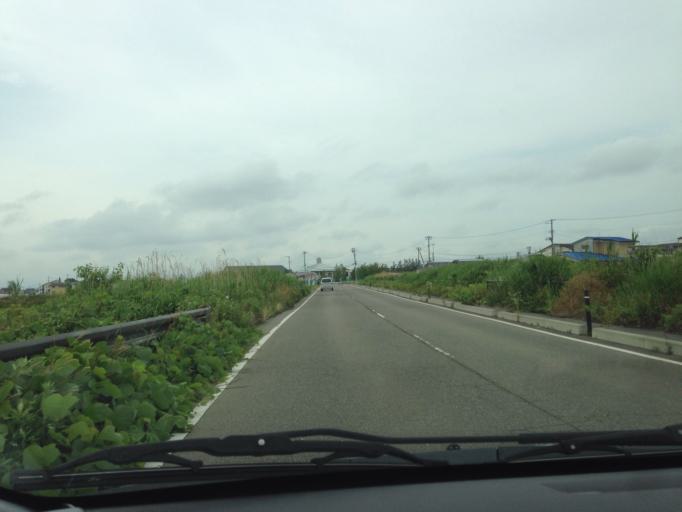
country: JP
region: Fukushima
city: Kitakata
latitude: 37.5693
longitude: 139.8891
